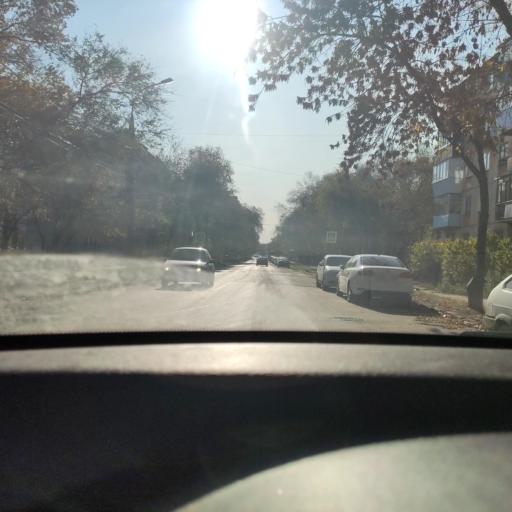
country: RU
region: Samara
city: Samara
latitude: 53.1939
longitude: 50.1739
